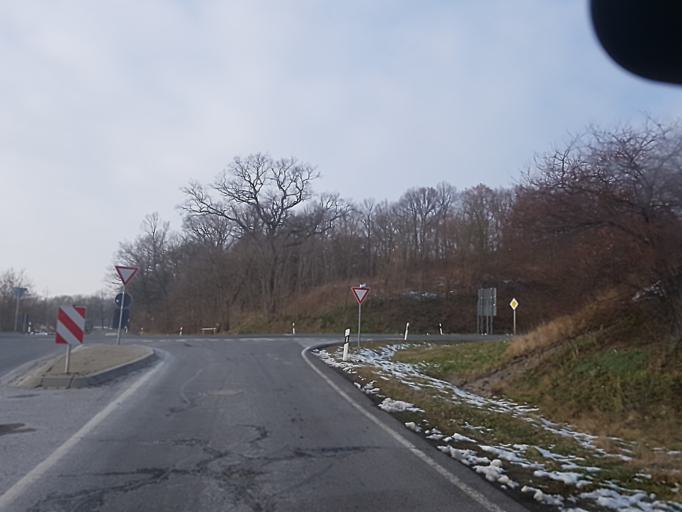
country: DE
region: Saxony
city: Leisnig
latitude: 51.1756
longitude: 12.9143
